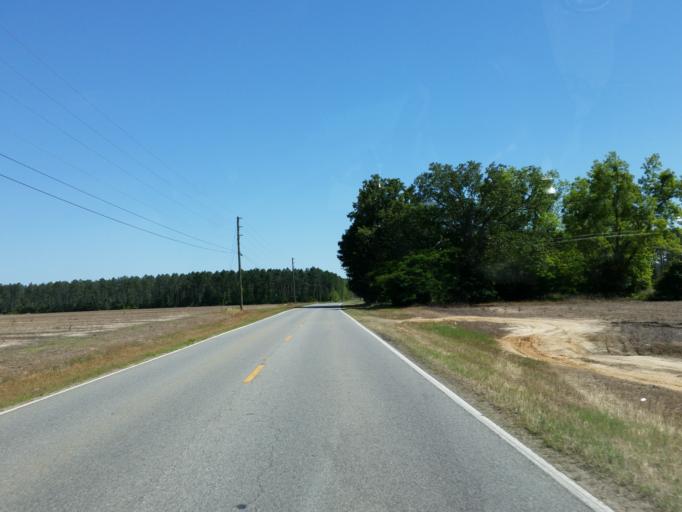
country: US
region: Georgia
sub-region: Cook County
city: Adel
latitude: 31.1028
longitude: -83.4114
